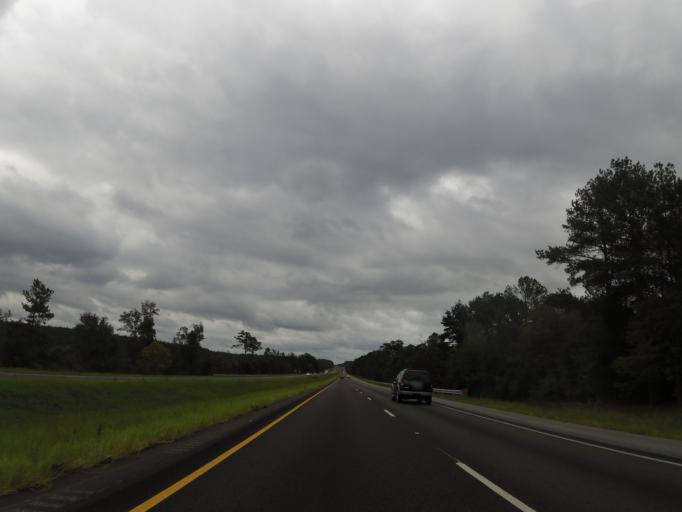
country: US
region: Alabama
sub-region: Conecuh County
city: Evergreen
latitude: 31.3627
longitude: -87.0626
